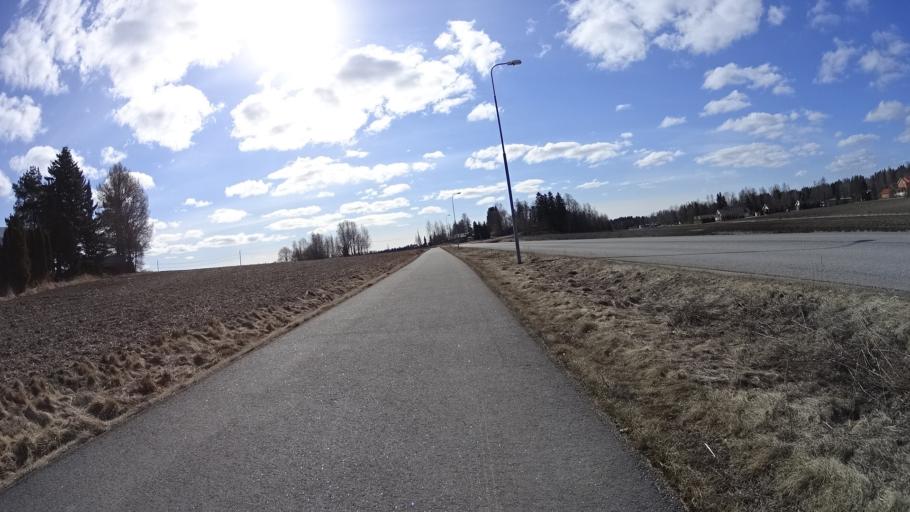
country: FI
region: Uusimaa
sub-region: Helsinki
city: Kauniainen
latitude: 60.2574
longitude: 24.7355
